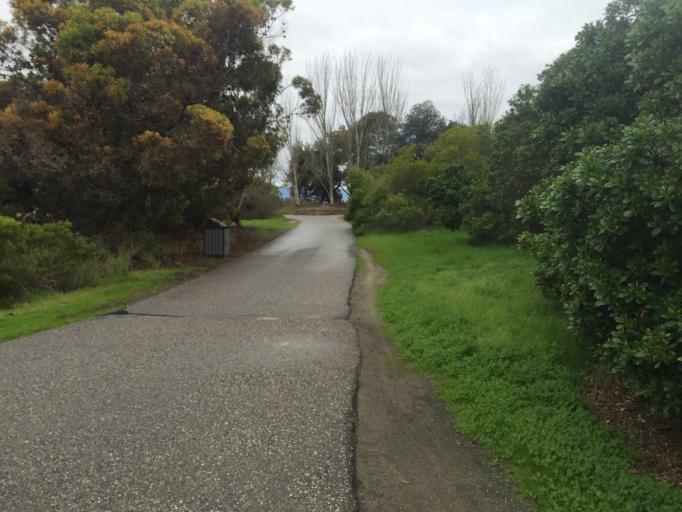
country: US
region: California
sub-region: Santa Clara County
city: Mountain View
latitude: 37.4331
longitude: -122.0869
